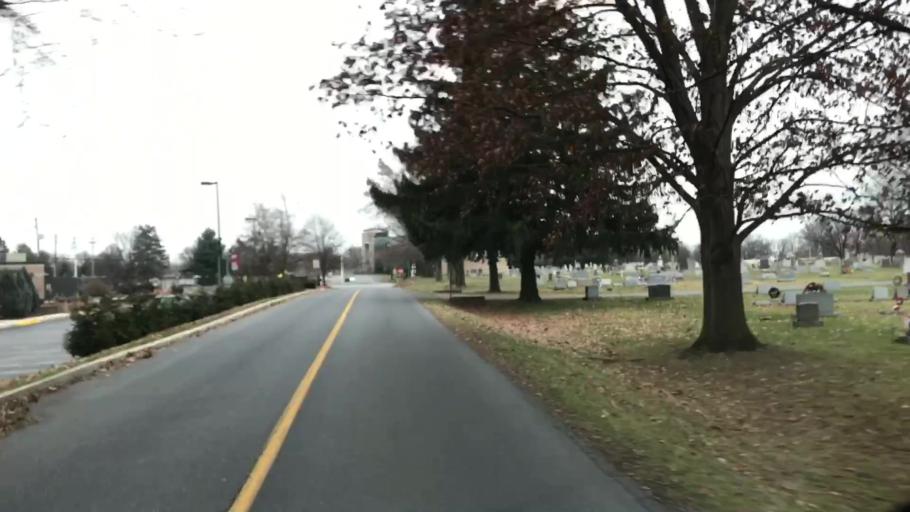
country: US
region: Pennsylvania
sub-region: Dauphin County
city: Highspire
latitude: 40.2174
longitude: -76.7926
